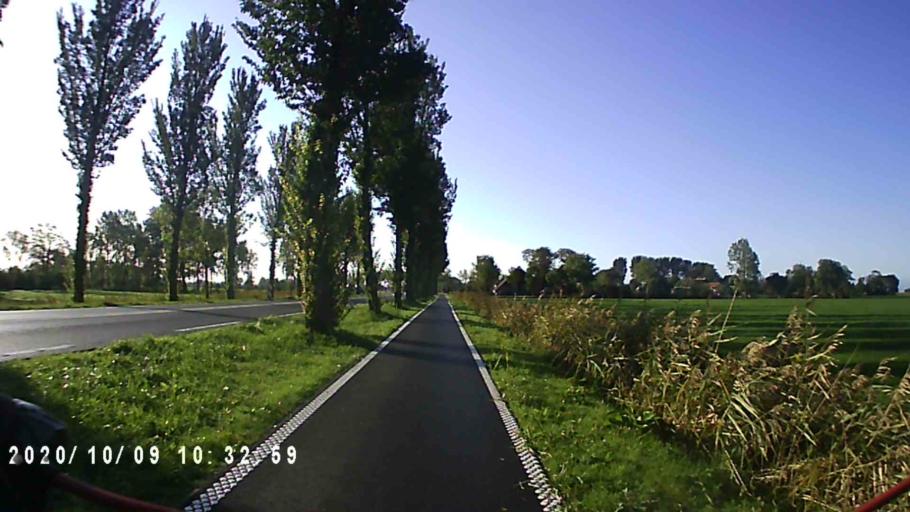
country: NL
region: Groningen
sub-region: Gemeente Winsum
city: Winsum
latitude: 53.3064
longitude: 6.5320
